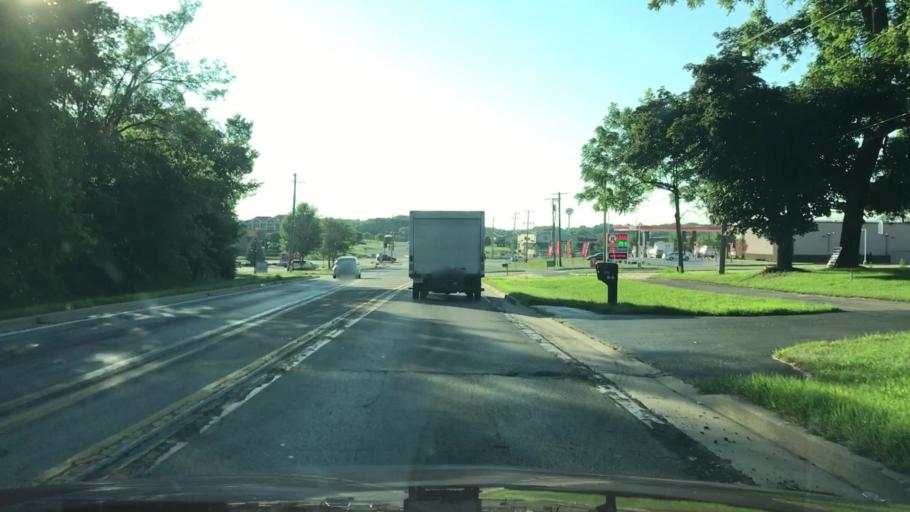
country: US
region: Illinois
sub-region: Winnebago County
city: Cherry Valley
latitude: 42.2425
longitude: -88.9825
